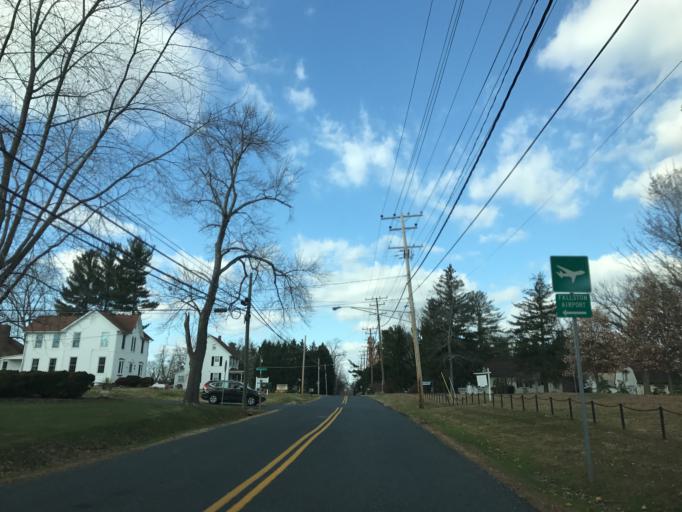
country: US
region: Maryland
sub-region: Harford County
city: Fallston
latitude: 39.5086
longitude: -76.4063
